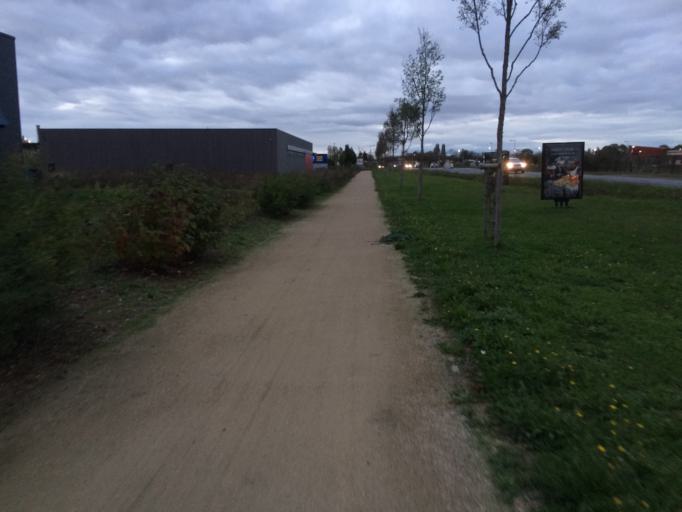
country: FR
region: Ile-de-France
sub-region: Departement de l'Essonne
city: Villejust
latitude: 48.6842
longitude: 2.2238
